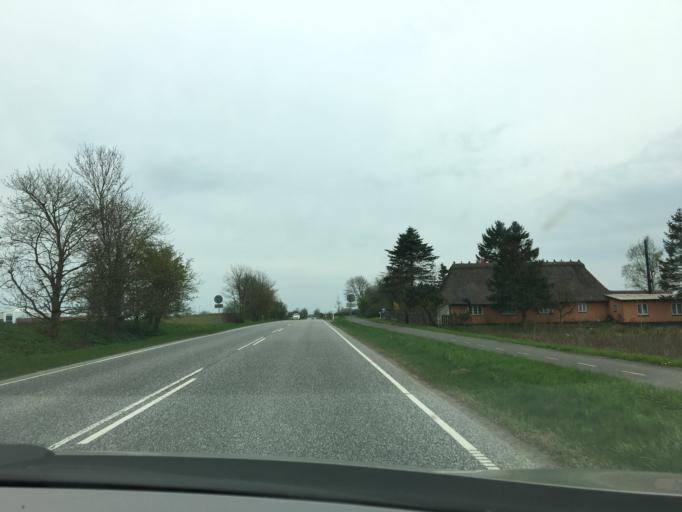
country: DK
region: South Denmark
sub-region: Vejle Kommune
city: Vejle
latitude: 55.7411
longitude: 9.5672
